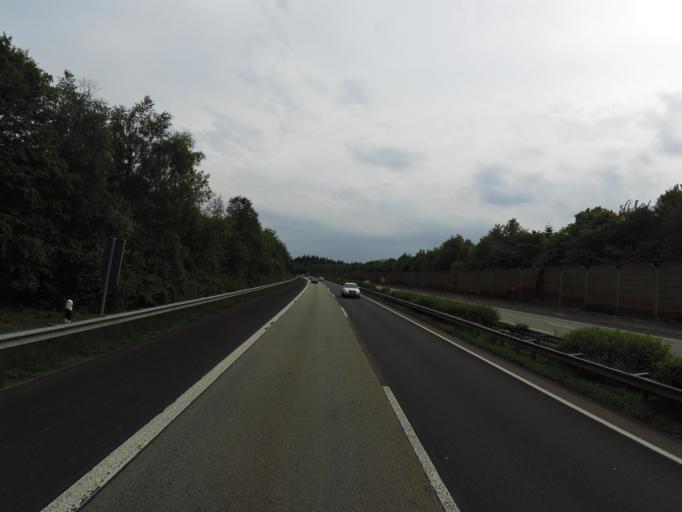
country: DE
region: Rheinland-Pfalz
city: Nortershausen
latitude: 50.2375
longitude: 7.5142
